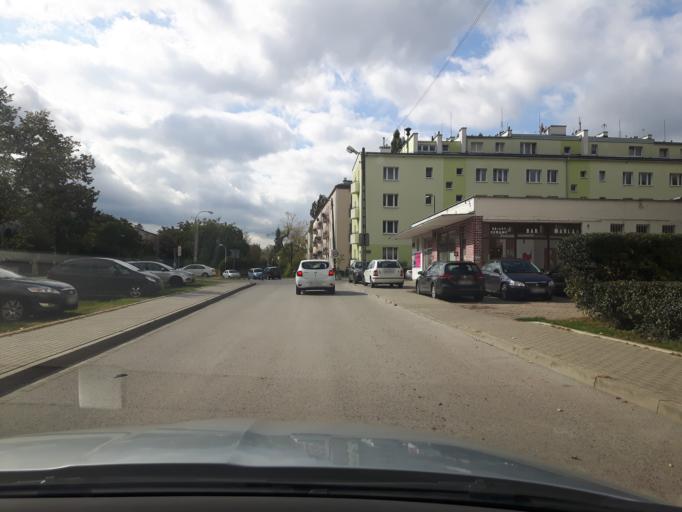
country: PL
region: Masovian Voivodeship
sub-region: Warszawa
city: Praga Poludnie
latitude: 52.2393
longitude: 21.0933
